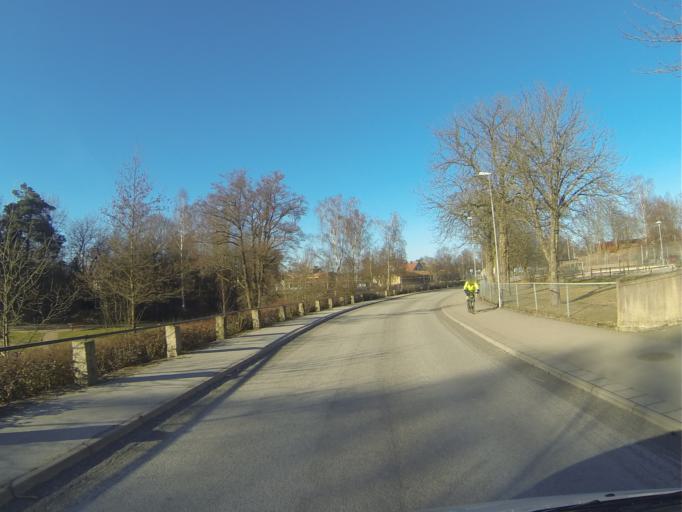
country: SE
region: Skane
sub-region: Hoors Kommun
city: Hoeoer
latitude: 55.9332
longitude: 13.5484
